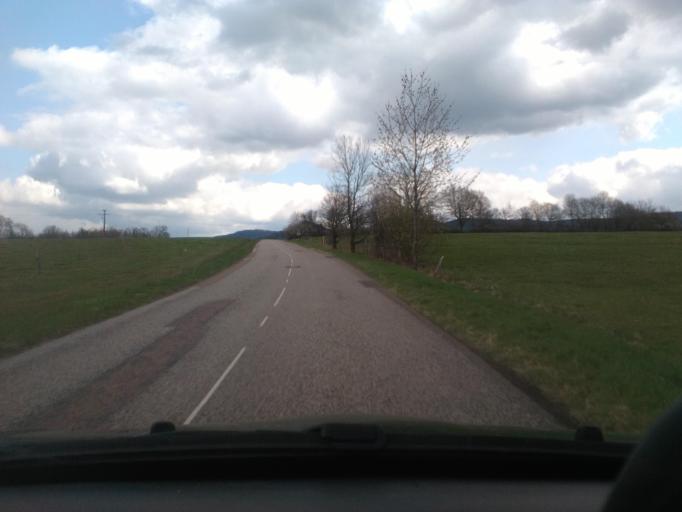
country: FR
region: Lorraine
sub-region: Departement des Vosges
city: Etival-Clairefontaine
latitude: 48.3313
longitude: 6.8239
